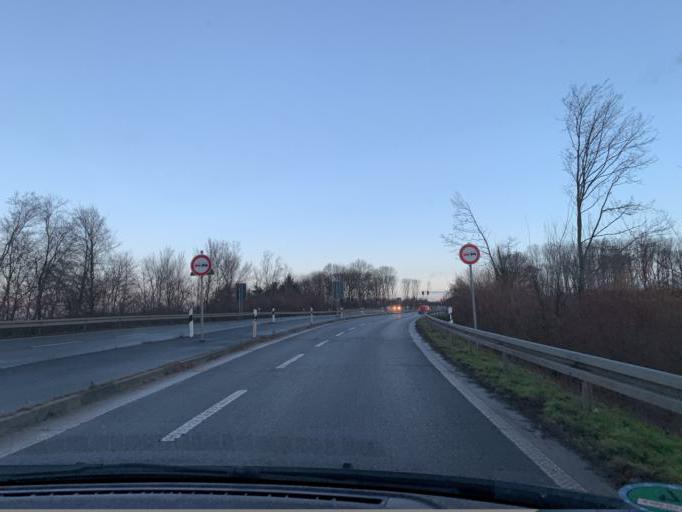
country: DE
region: North Rhine-Westphalia
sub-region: Regierungsbezirk Dusseldorf
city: Juchen
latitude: 51.1022
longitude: 6.5334
